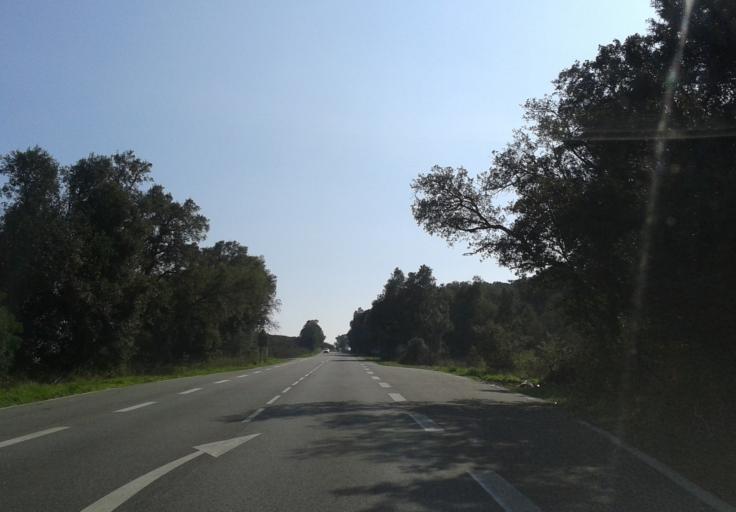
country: FR
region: Corsica
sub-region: Departement de la Haute-Corse
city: Linguizzetta
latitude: 42.2307
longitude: 9.5444
